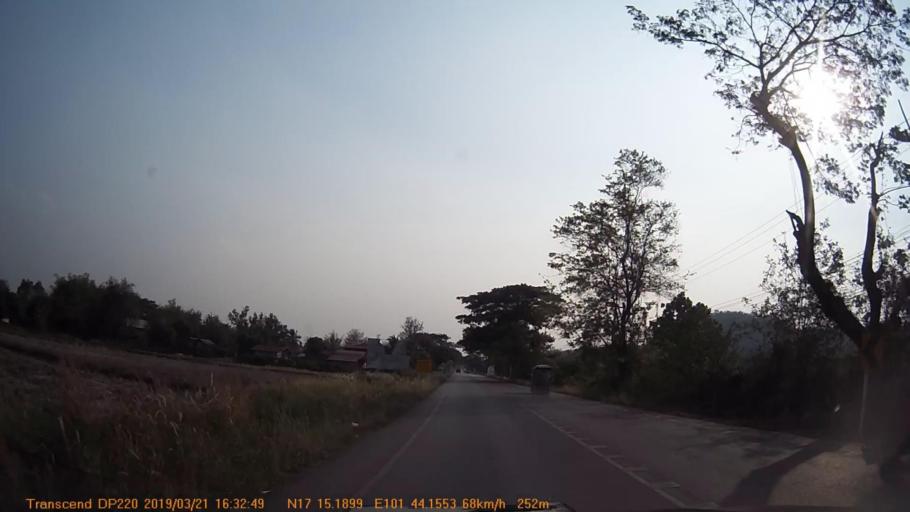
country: TH
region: Loei
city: Wang Saphung
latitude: 17.2529
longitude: 101.7356
